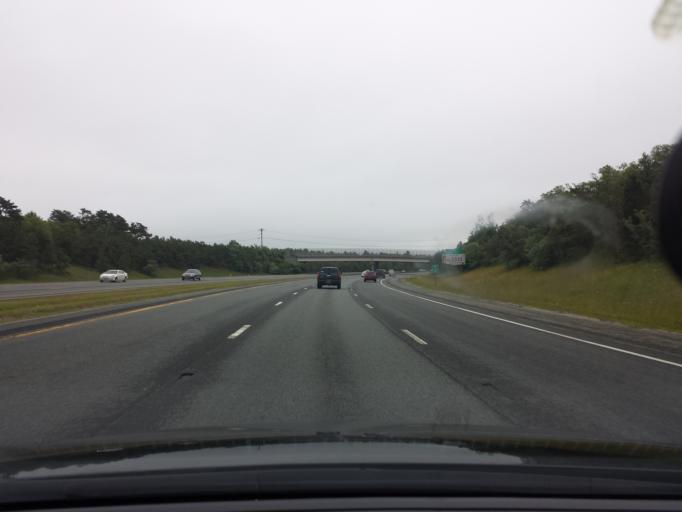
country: US
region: Massachusetts
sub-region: Barnstable County
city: Bourne
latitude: 41.7763
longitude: -70.5876
